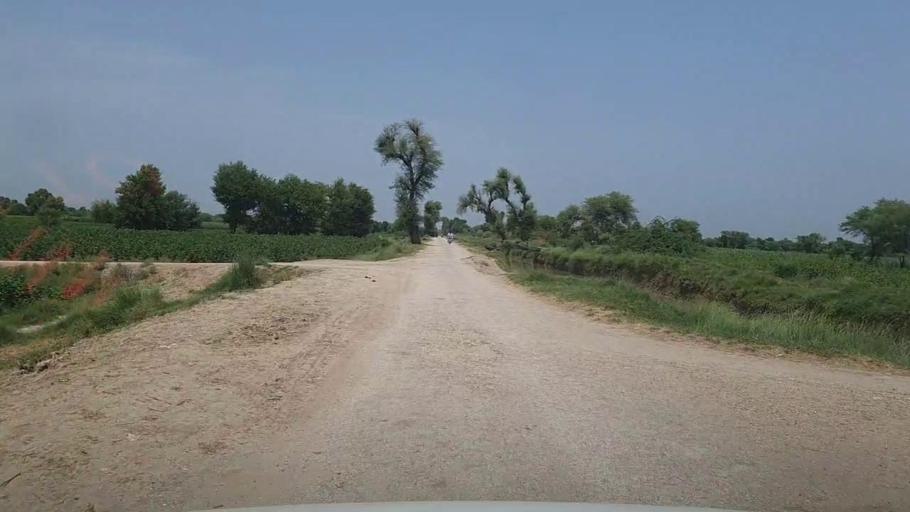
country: PK
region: Sindh
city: Karaundi
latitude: 26.8898
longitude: 68.3333
